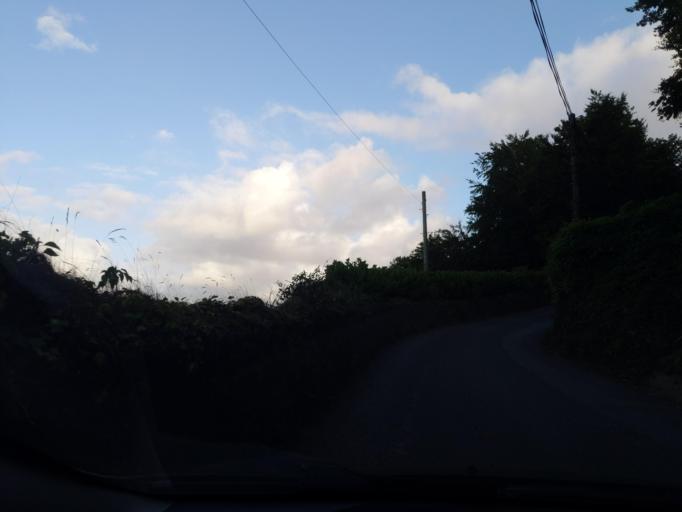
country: GB
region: England
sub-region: Devon
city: Salcombe
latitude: 50.2295
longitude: -3.7824
